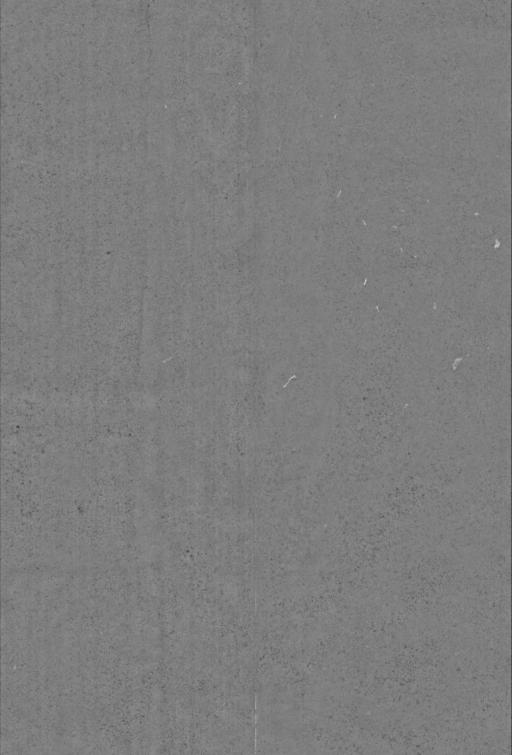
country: US
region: Maryland
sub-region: Prince George's County
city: Silver Hill
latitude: 38.8674
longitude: -76.9531
